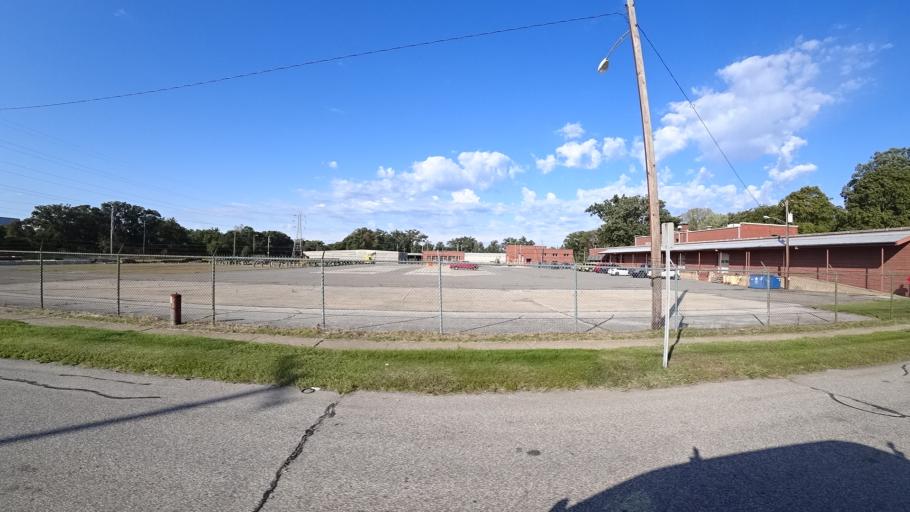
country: US
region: Indiana
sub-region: LaPorte County
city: Trail Creek
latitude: 41.7015
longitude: -86.8746
